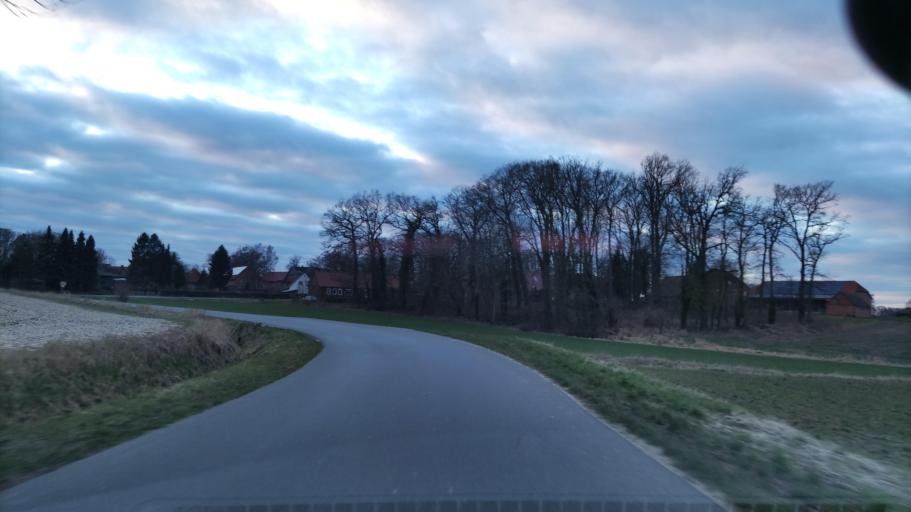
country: DE
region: Lower Saxony
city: Natendorf
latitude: 53.0566
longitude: 10.4583
